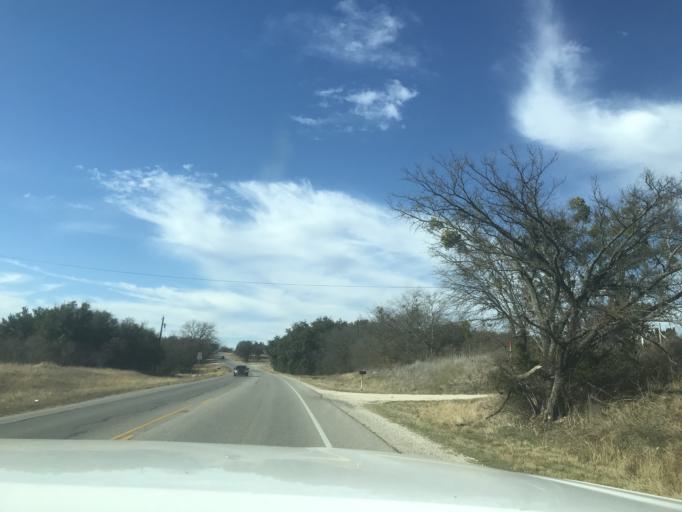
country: US
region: Texas
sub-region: Erath County
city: Stephenville
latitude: 32.2049
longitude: -98.1872
